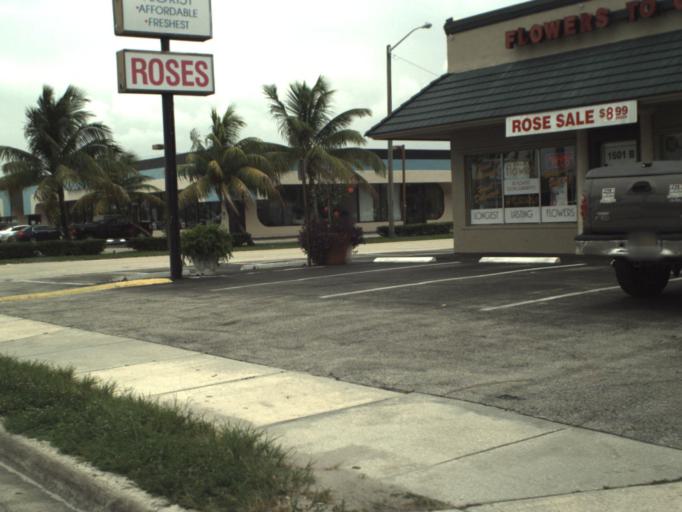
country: US
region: Florida
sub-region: Palm Beach County
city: Haverhill
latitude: 26.7011
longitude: -80.1115
